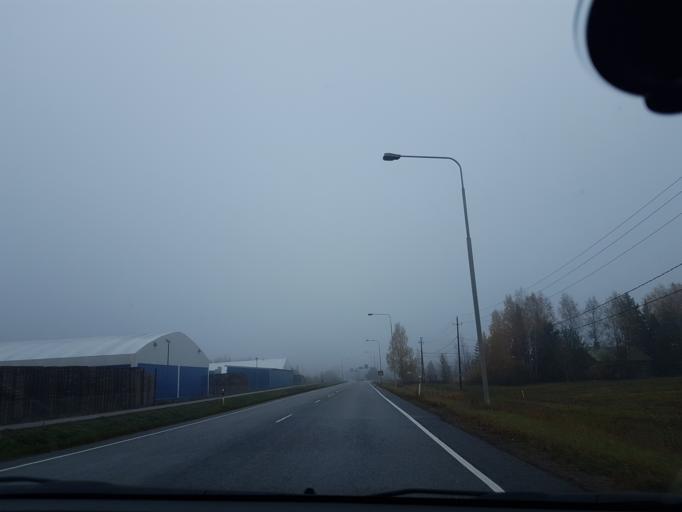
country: FI
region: Uusimaa
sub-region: Helsinki
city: Jaervenpaeae
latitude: 60.4666
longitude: 25.1405
